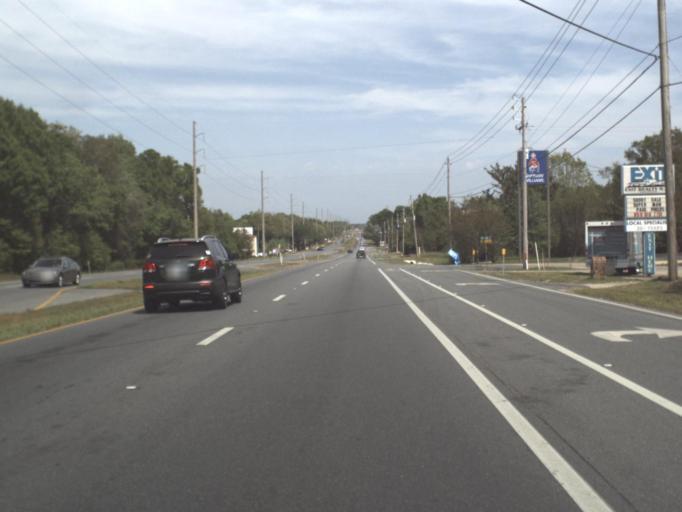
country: US
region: Florida
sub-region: Santa Rosa County
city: Pace
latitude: 30.6029
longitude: -87.1018
